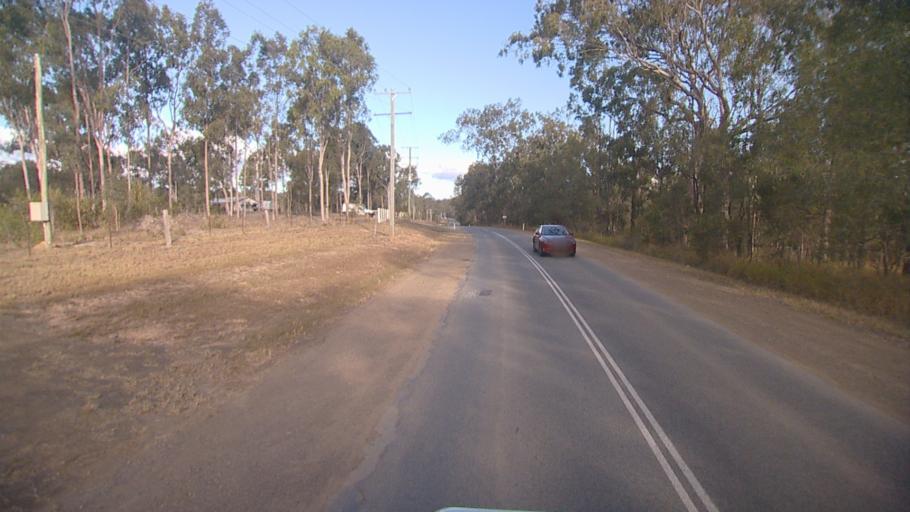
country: AU
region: Queensland
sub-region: Logan
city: Cedar Vale
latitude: -27.8561
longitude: 153.0534
